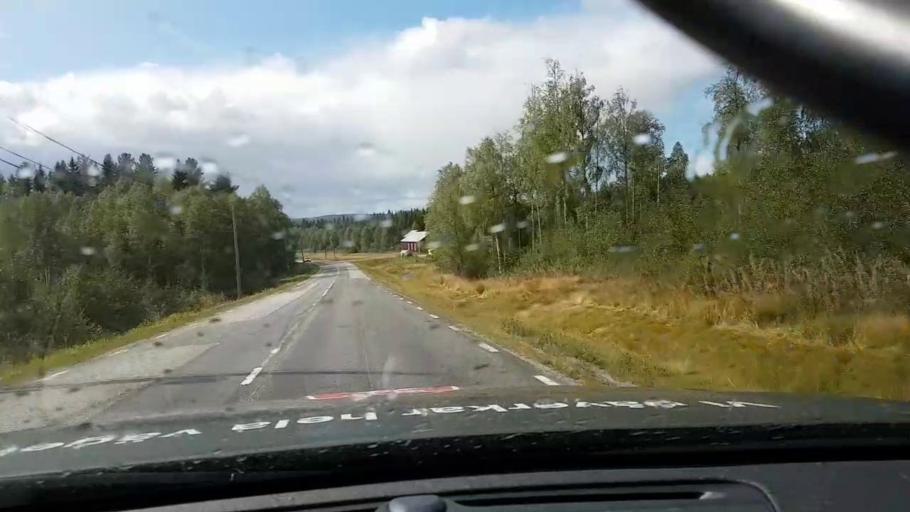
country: SE
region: Vaesterbotten
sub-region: Asele Kommun
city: Asele
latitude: 63.7919
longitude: 17.6155
